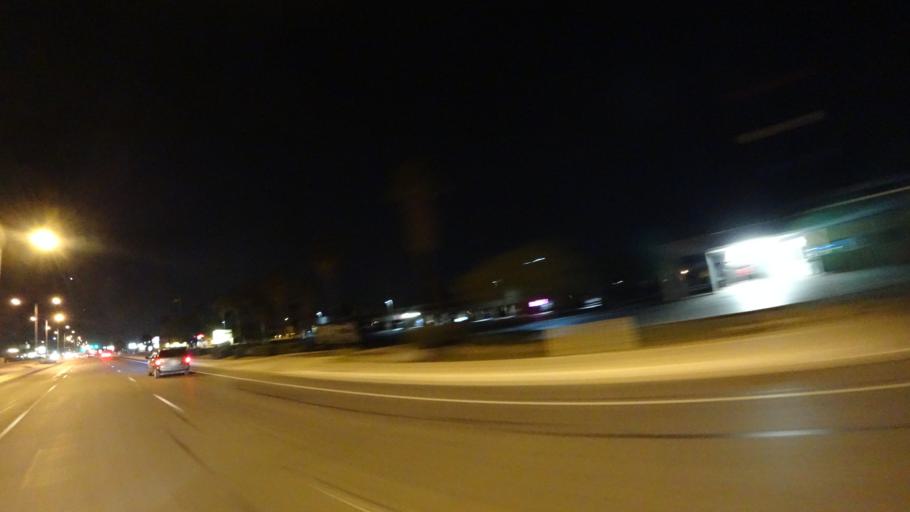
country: US
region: Arizona
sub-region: Maricopa County
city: Gilbert
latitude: 33.4156
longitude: -111.7237
